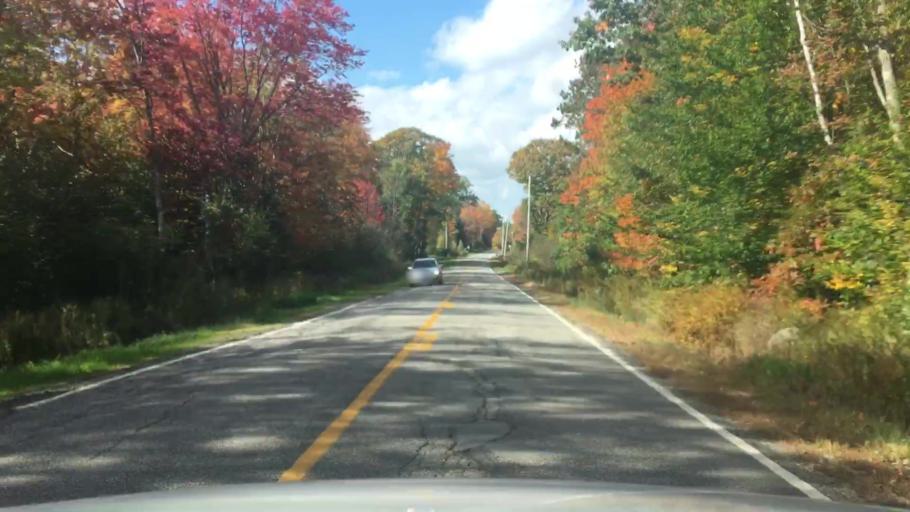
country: US
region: Maine
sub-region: Knox County
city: Appleton
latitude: 44.2732
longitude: -69.2841
